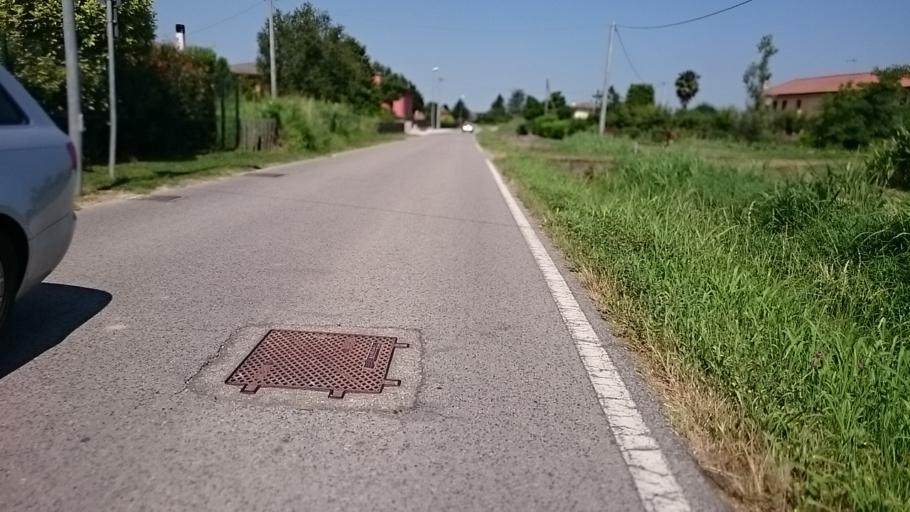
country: IT
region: Veneto
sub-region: Provincia di Venezia
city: Fosso
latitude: 45.3697
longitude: 12.0363
